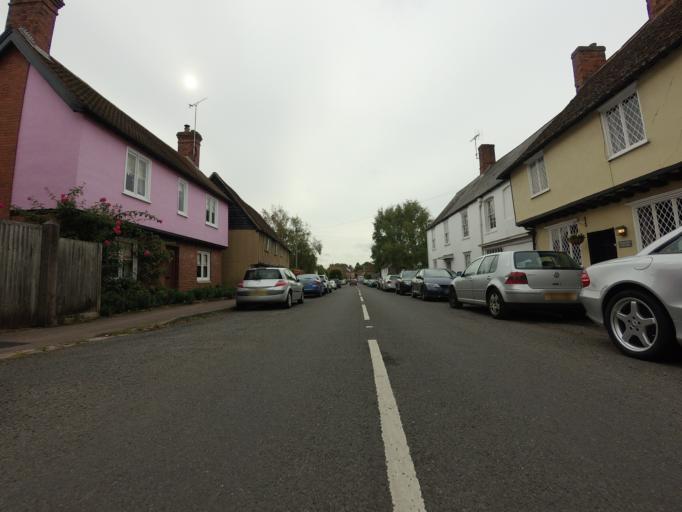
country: GB
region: England
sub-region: Hertfordshire
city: Reed
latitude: 52.0017
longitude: 0.0154
